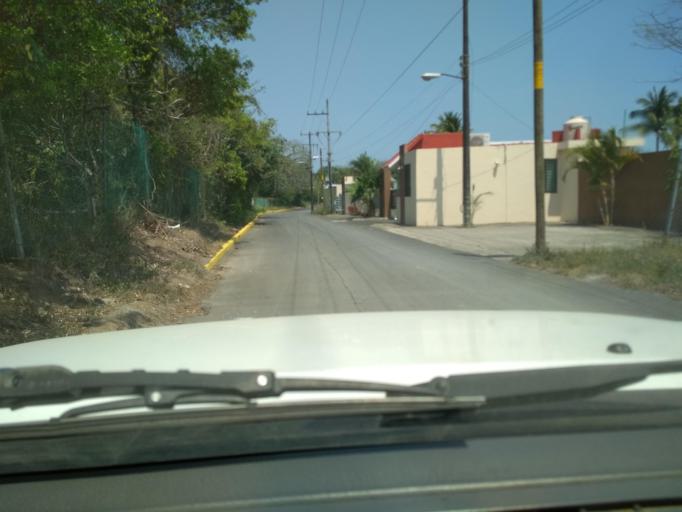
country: MX
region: Veracruz
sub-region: Medellin
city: Fraccionamiento Arboledas San Ramon
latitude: 19.0893
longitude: -96.1428
